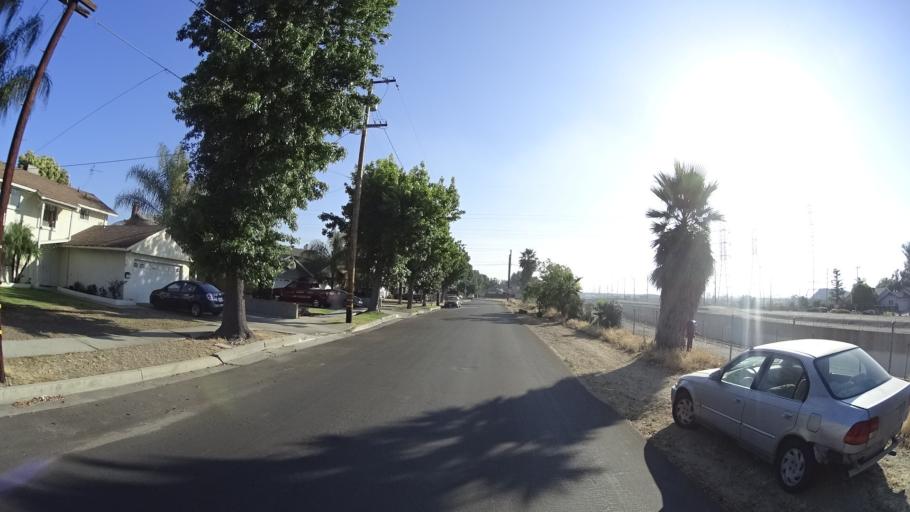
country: US
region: California
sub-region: Los Angeles County
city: Van Nuys
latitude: 34.2252
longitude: -118.4212
